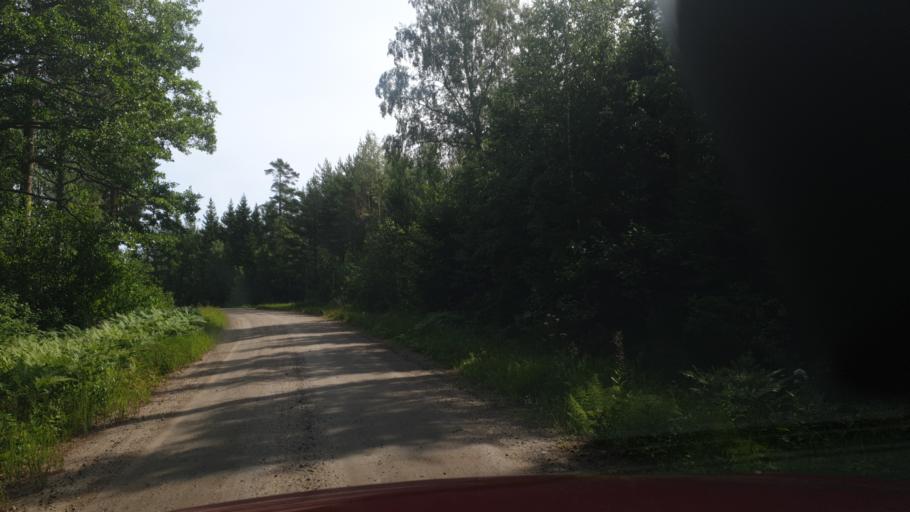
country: SE
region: Gaevleborg
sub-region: Hudiksvalls Kommun
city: Hudiksvall
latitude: 61.6379
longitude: 17.4481
